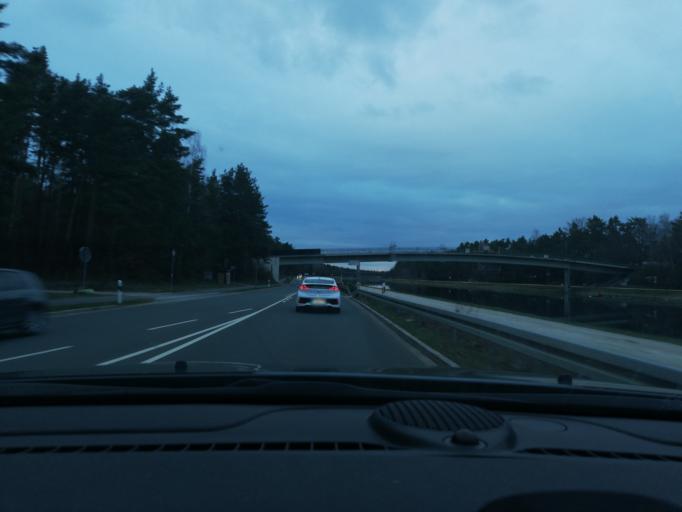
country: DE
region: Bavaria
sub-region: Regierungsbezirk Mittelfranken
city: Mohrendorf
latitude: 49.6070
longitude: 10.9719
